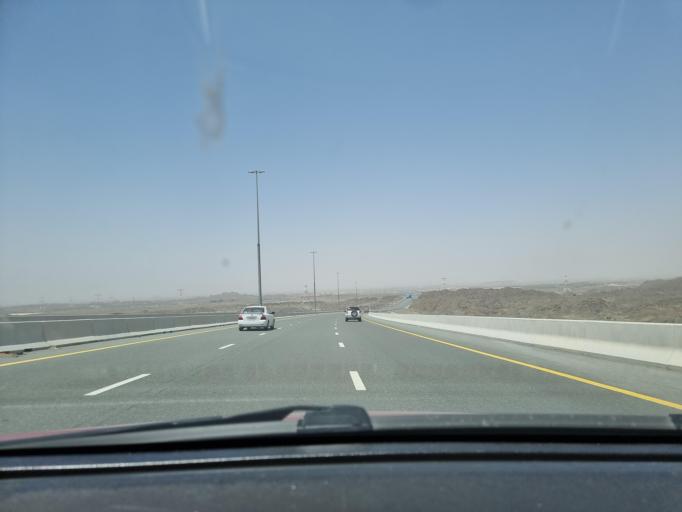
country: AE
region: Ash Shariqah
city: Adh Dhayd
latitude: 25.1588
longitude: 56.0474
